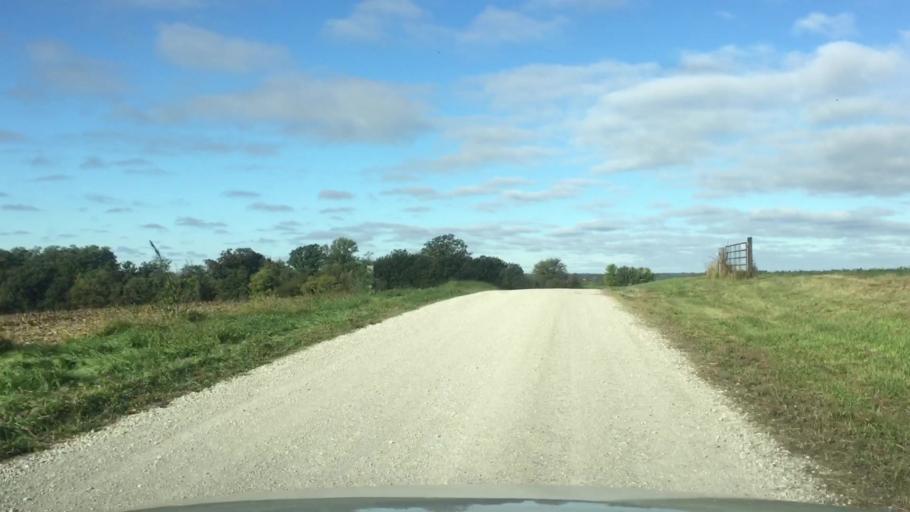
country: US
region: Missouri
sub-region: Howard County
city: New Franklin
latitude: 39.0791
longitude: -92.7486
